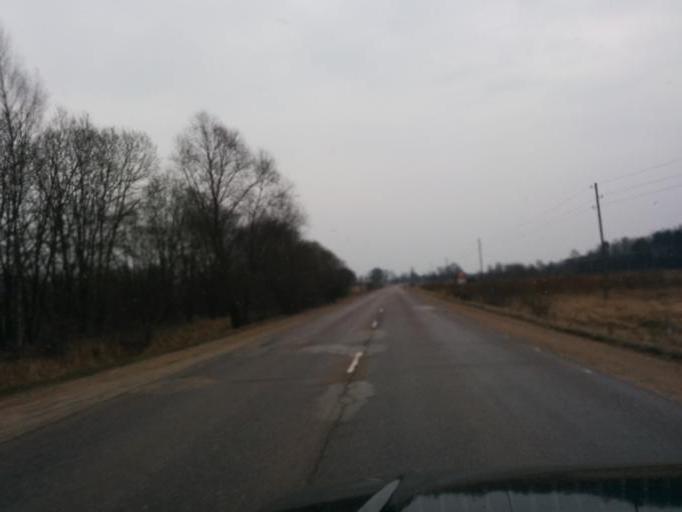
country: LV
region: Ikskile
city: Ikskile
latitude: 56.8211
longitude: 24.4351
